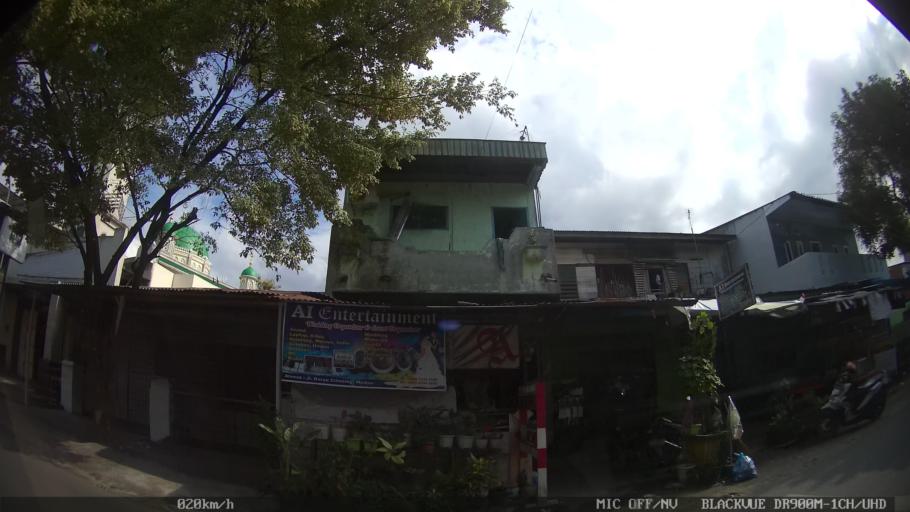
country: ID
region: North Sumatra
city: Medan
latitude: 3.6207
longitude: 98.6667
